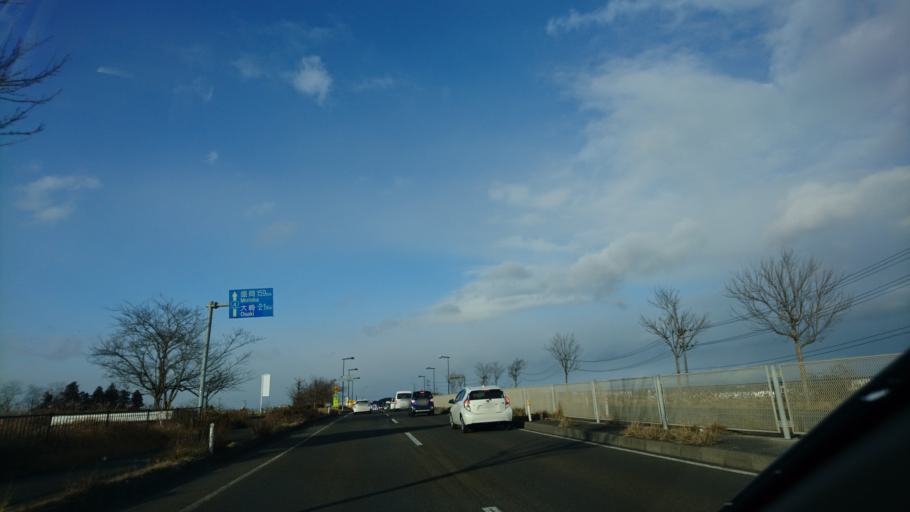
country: JP
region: Miyagi
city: Tomiya
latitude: 38.4300
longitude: 140.8911
